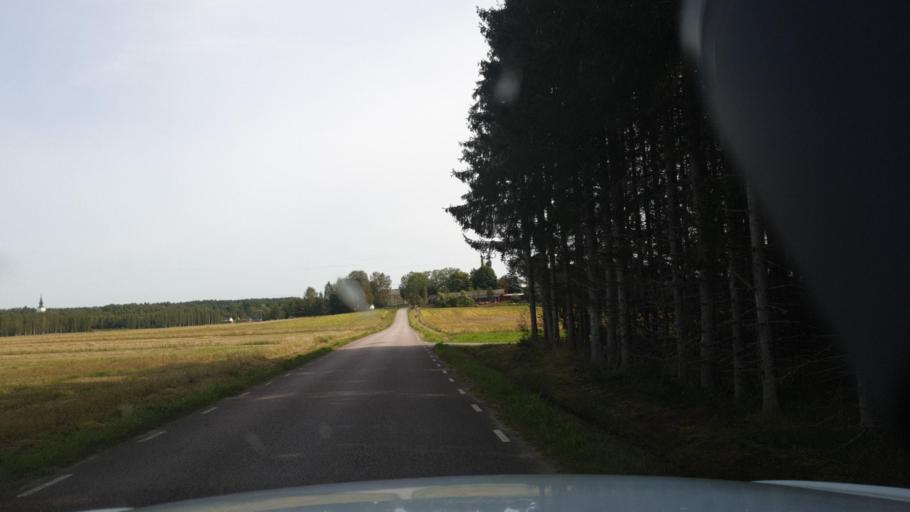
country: SE
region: Vaermland
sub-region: Arvika Kommun
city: Arvika
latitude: 59.5487
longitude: 12.5474
